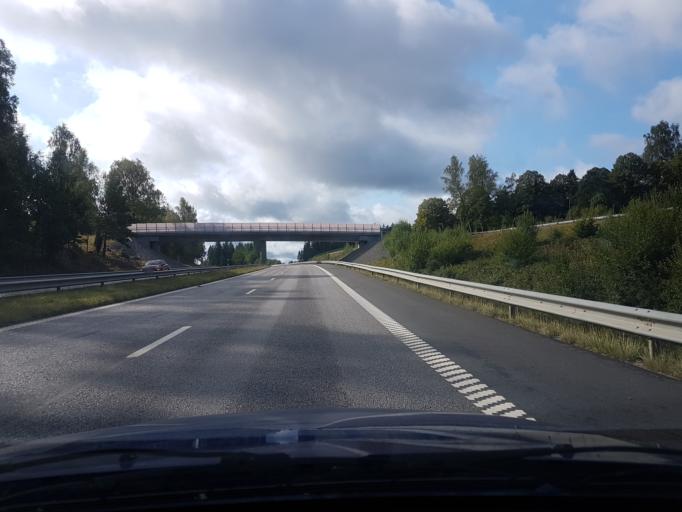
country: SE
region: Vaestra Goetaland
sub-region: Alingsas Kommun
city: Ingared
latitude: 57.8861
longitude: 12.4891
